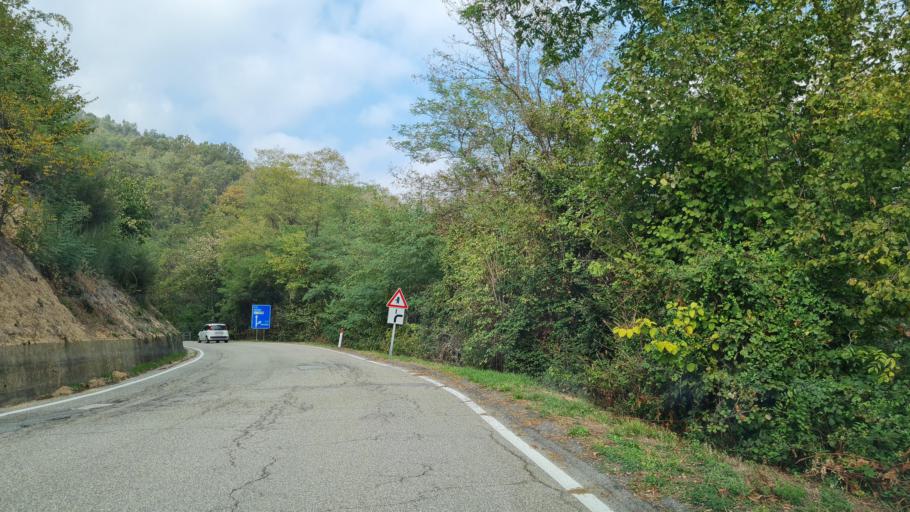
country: IT
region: Piedmont
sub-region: Provincia di Biella
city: Mezzana Mortigliengo
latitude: 45.6261
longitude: 8.1835
